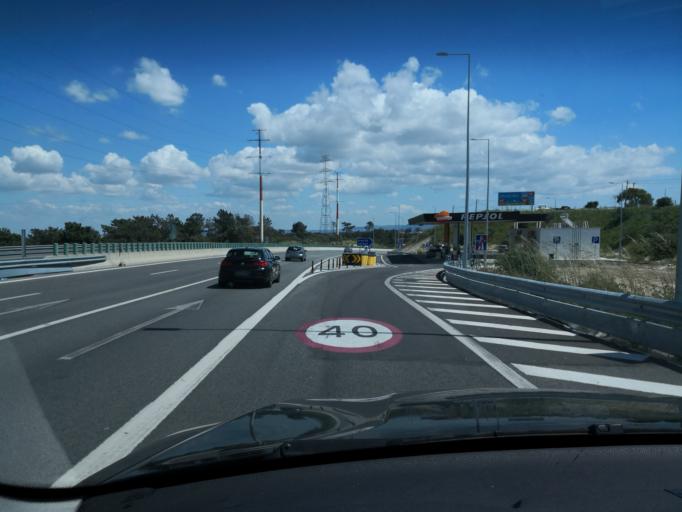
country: PT
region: Setubal
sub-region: Almada
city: Sobreda
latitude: 38.6385
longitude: -9.1994
